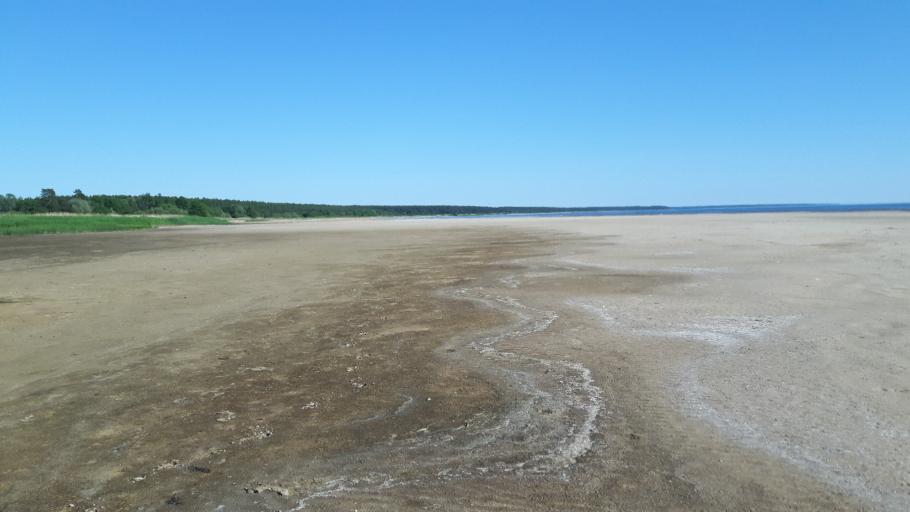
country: LV
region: Salacgrivas
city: Salacgriva
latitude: 57.6983
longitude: 24.3437
